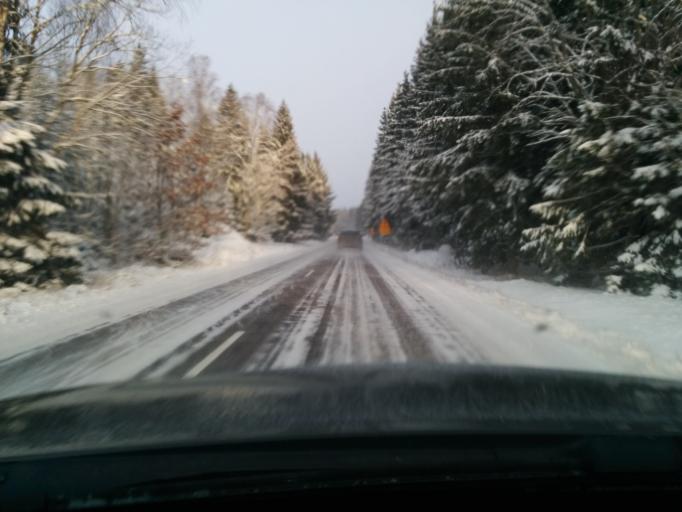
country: SE
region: Uppsala
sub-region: Tierps Kommun
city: Orbyhus
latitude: 60.2141
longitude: 17.7009
